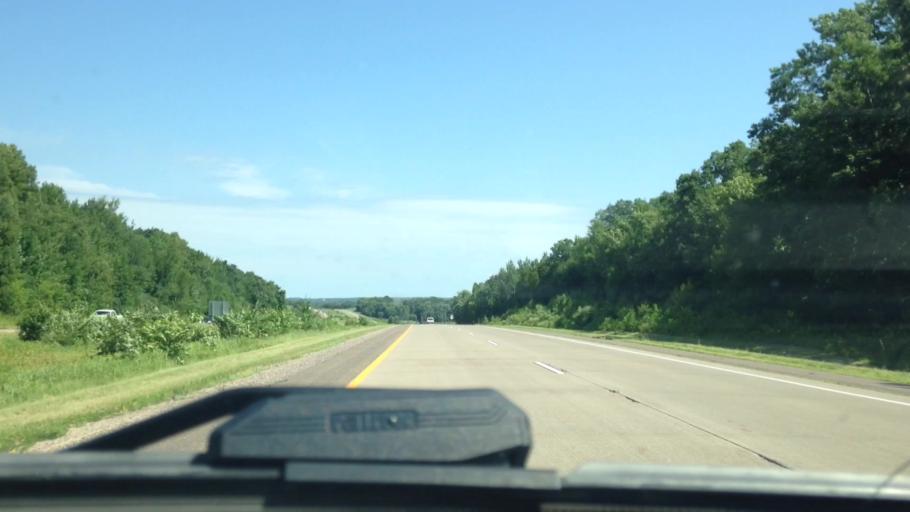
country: US
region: Wisconsin
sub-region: Barron County
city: Rice Lake
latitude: 45.5198
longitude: -91.7597
